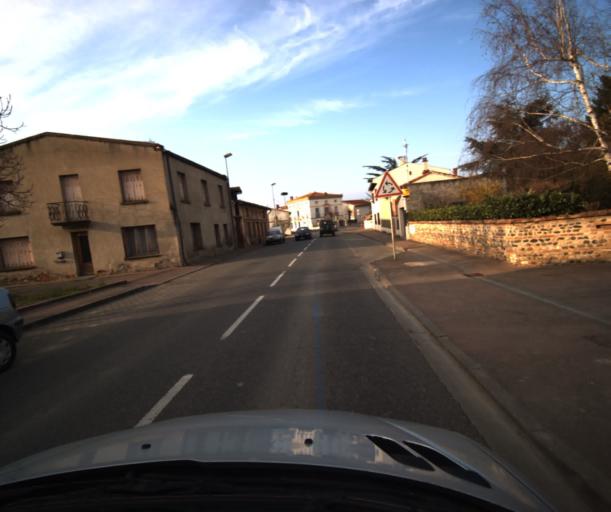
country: FR
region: Midi-Pyrenees
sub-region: Departement de la Haute-Garonne
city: Launaguet
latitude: 43.6759
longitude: 1.4562
